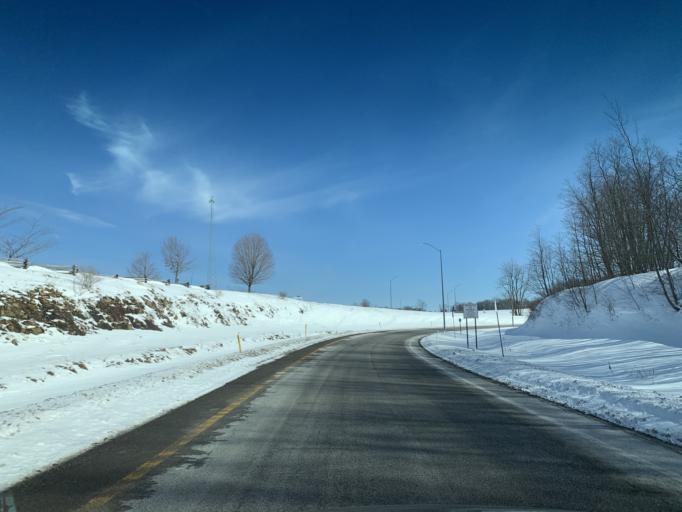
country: US
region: West Virginia
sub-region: Preston County
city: Terra Alta
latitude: 39.6631
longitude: -79.4954
